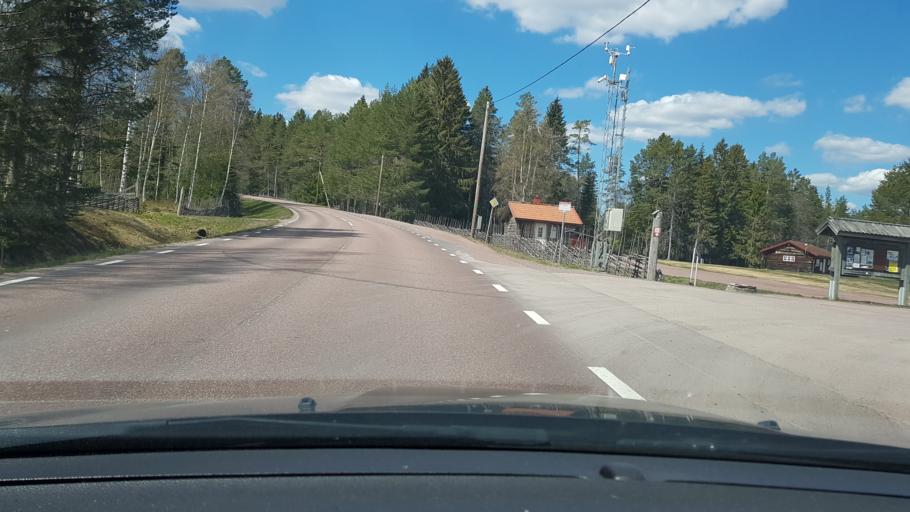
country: SE
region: Dalarna
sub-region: Malung-Saelens kommun
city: Malung
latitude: 61.0787
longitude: 13.6205
